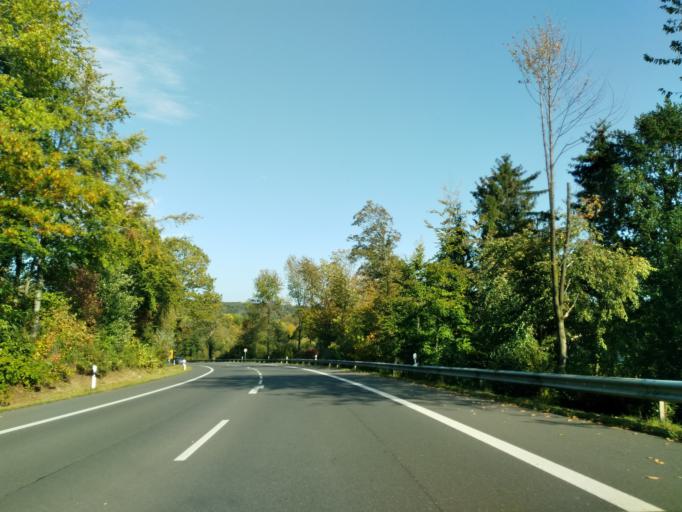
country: DE
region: North Rhine-Westphalia
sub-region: Regierungsbezirk Koln
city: Hennef
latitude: 50.7007
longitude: 7.2851
